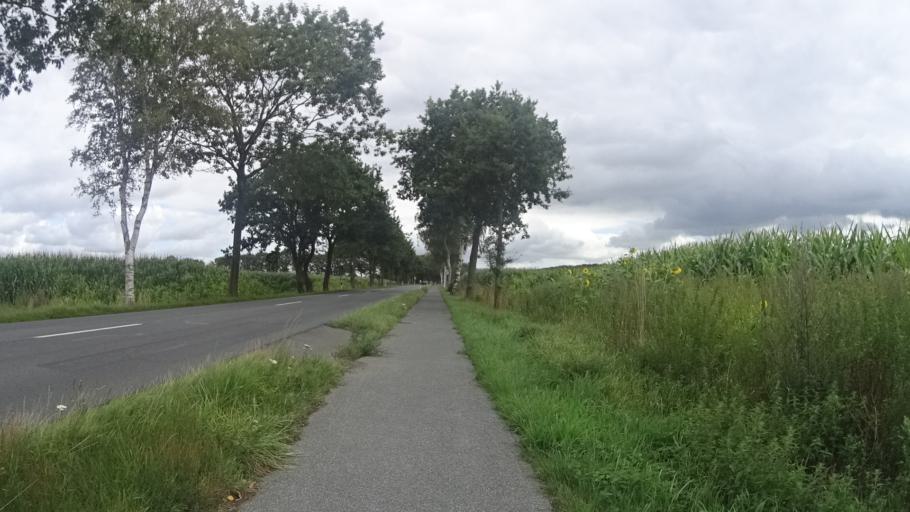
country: DE
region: Lower Saxony
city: Schiffdorf
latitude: 53.5383
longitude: 8.6730
